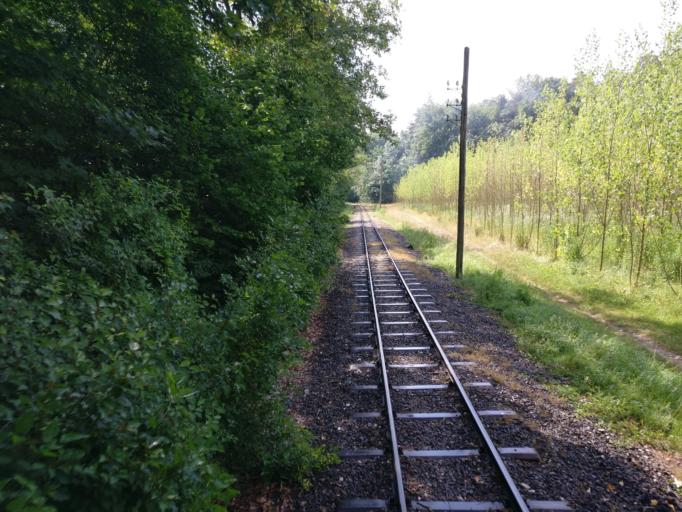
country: AT
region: Upper Austria
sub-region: Politischer Bezirk Steyr-Land
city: Garsten
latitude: 48.0458
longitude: 14.3688
